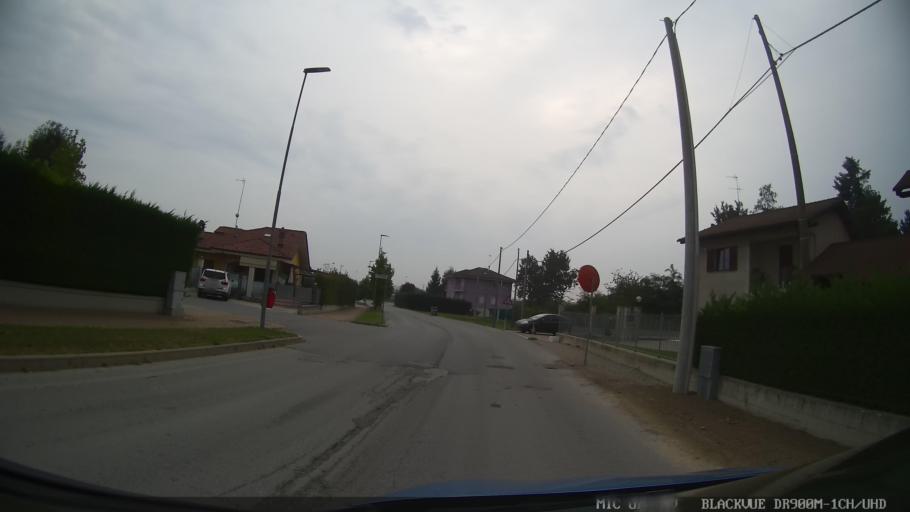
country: IT
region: Piedmont
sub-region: Provincia di Cuneo
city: Fossano
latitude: 44.5729
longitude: 7.7456
